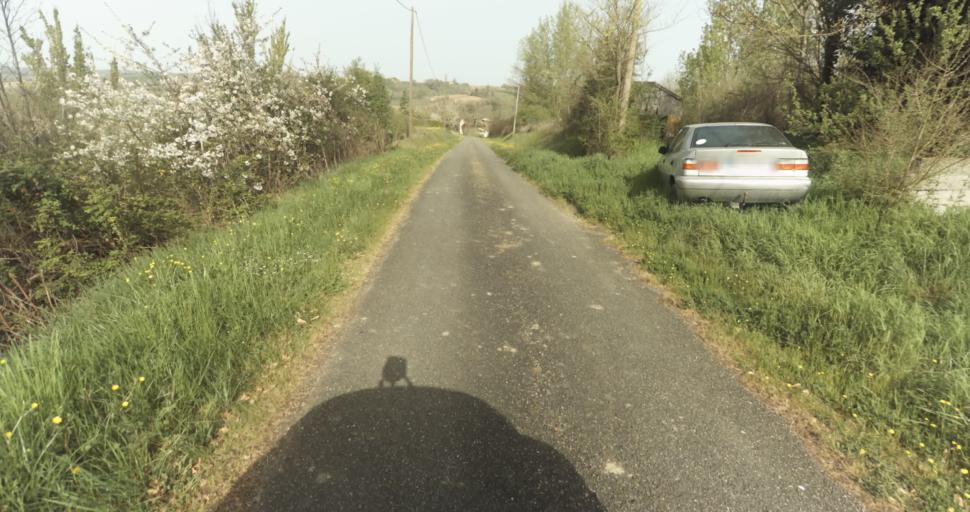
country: FR
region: Midi-Pyrenees
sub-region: Departement du Tarn-et-Garonne
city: Moissac
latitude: 44.1663
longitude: 1.0408
